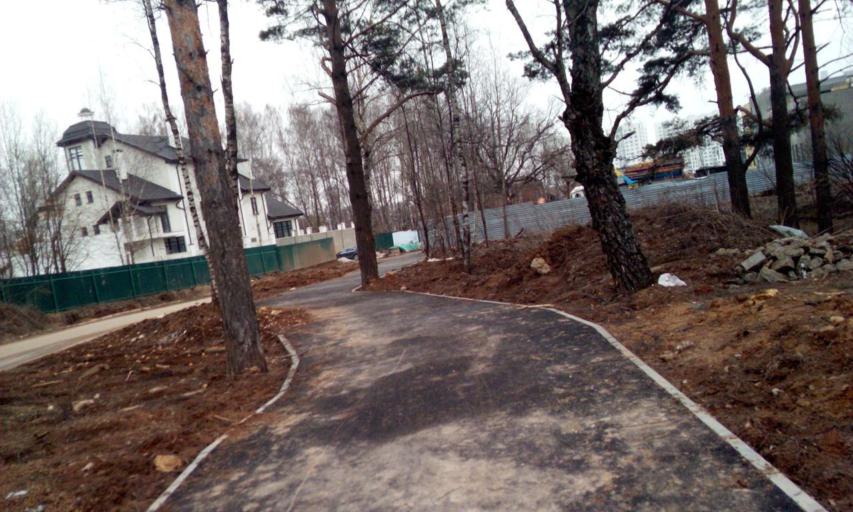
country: RU
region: Moskovskaya
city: Kommunarka
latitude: 55.5556
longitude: 37.5172
